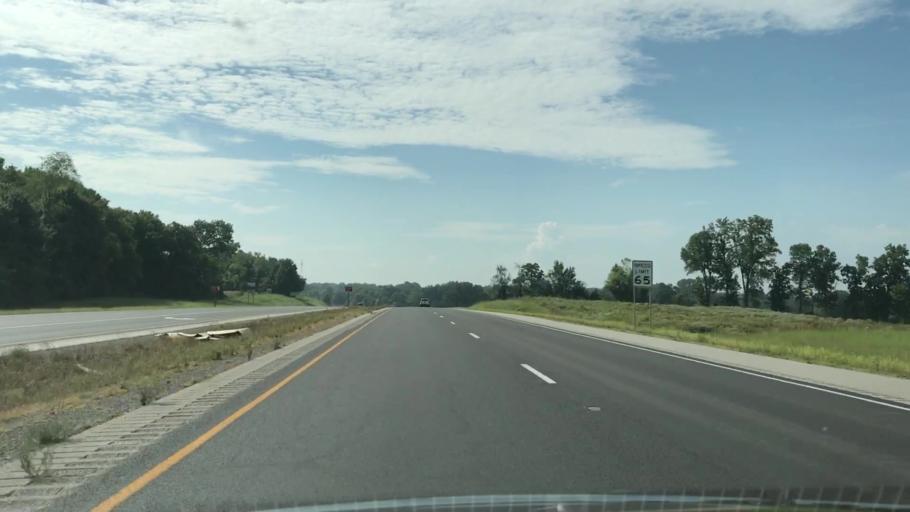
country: US
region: Kentucky
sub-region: Warren County
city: Plano
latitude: 36.8726
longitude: -86.3543
